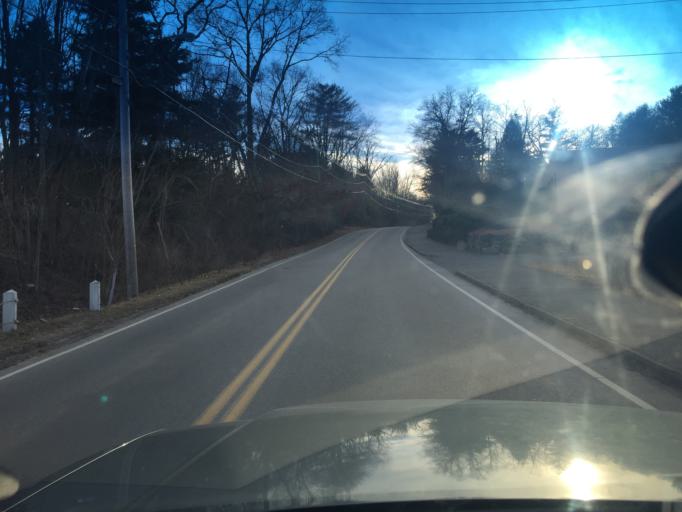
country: US
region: Massachusetts
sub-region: Middlesex County
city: Holliston
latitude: 42.2090
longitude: -71.4181
